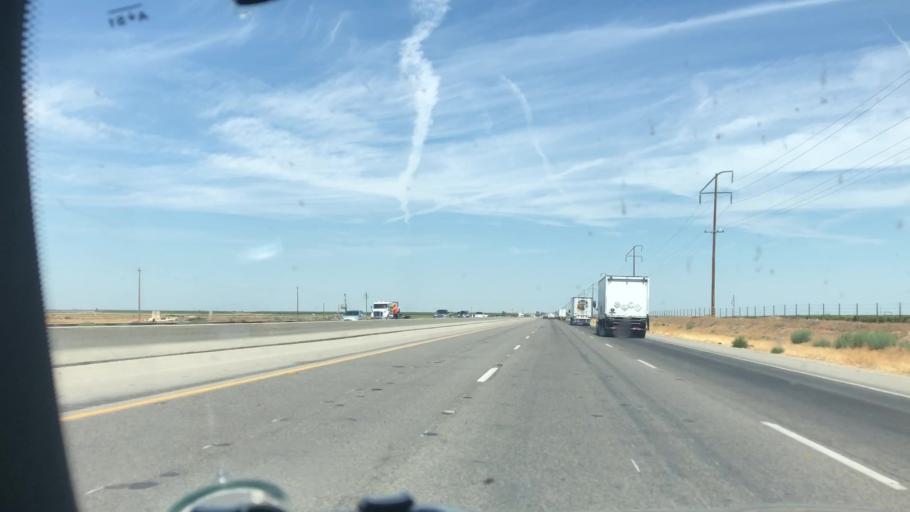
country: US
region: California
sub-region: Kern County
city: Greenacres
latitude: 35.4601
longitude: -119.1118
